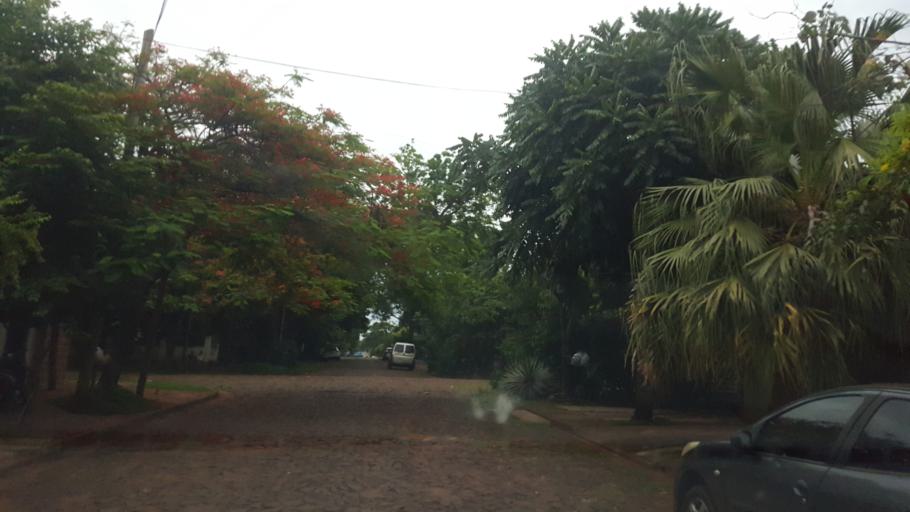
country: AR
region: Misiones
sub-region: Departamento de Capital
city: Posadas
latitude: -27.3646
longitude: -55.9295
